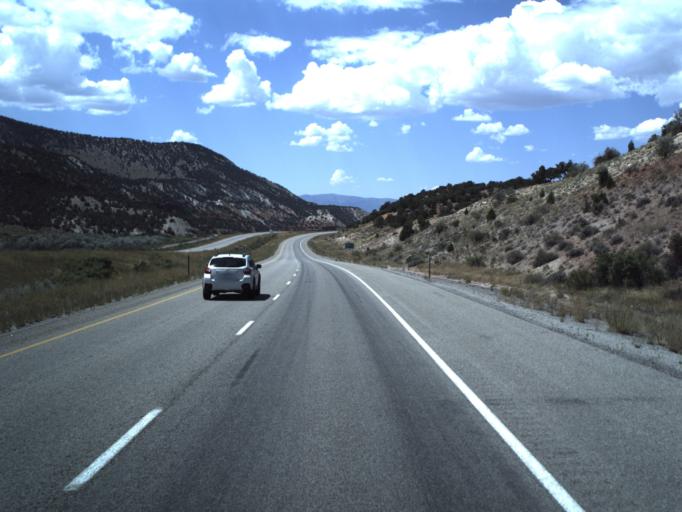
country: US
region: Utah
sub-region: Sevier County
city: Salina
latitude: 38.9207
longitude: -111.7559
